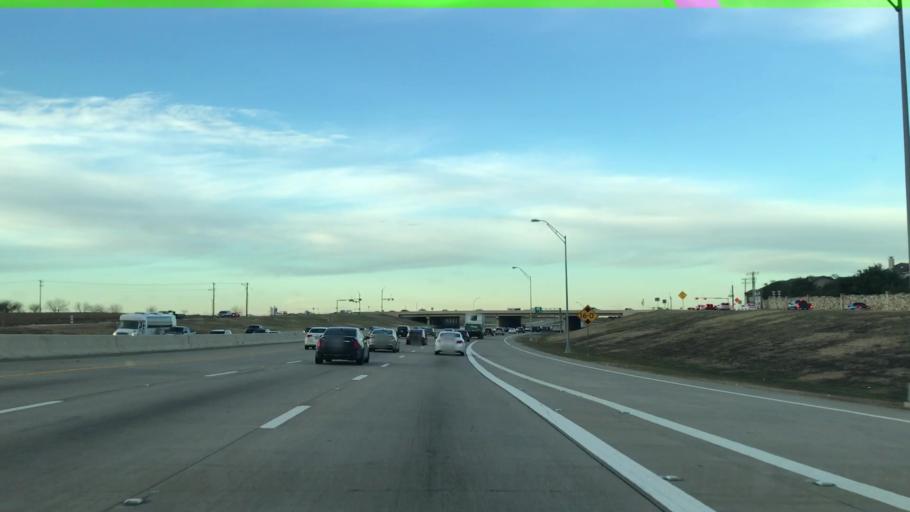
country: US
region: Texas
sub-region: Denton County
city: The Colony
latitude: 33.0434
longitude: -96.9227
